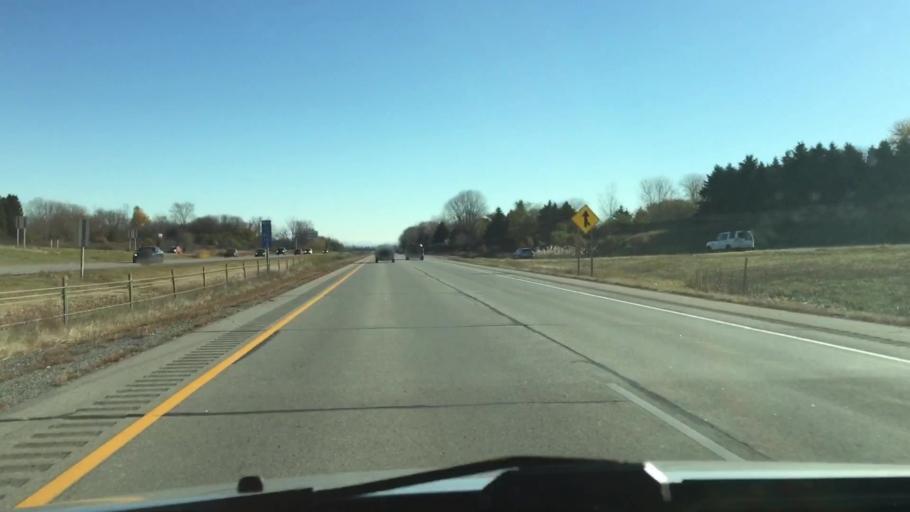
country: US
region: Wisconsin
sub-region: Outagamie County
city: Appleton
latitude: 44.2985
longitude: -88.4135
